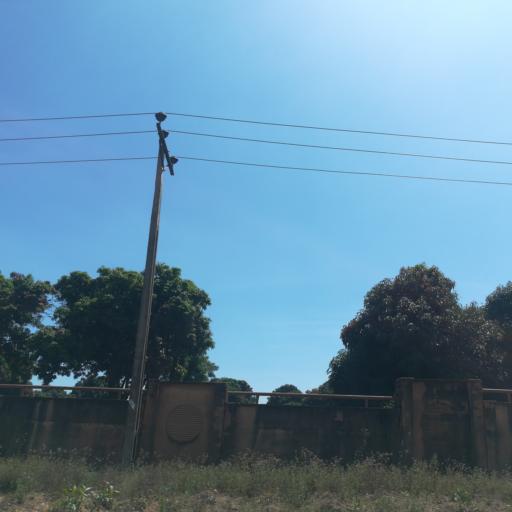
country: NG
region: Plateau
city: Bukuru
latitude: 9.8033
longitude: 8.8694
